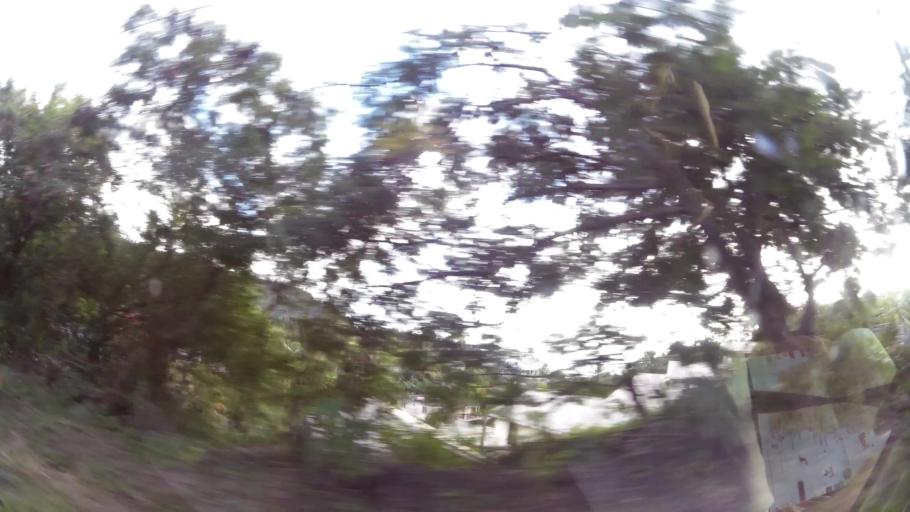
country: DM
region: Saint Joseph
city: Saint Joseph
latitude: 15.3990
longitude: -61.4250
